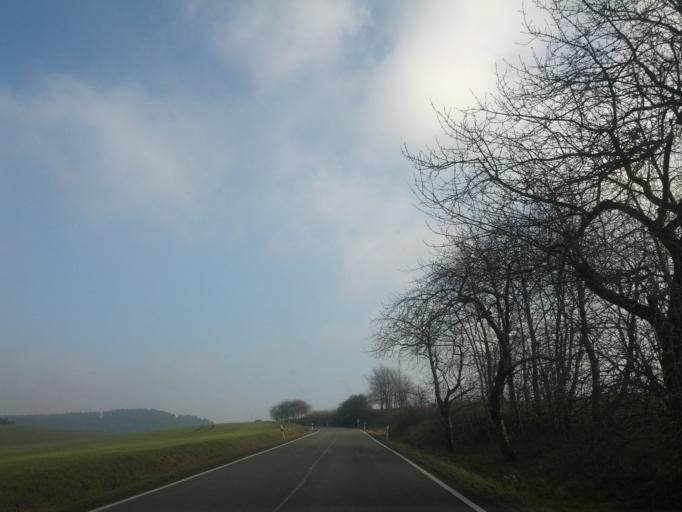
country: DE
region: Thuringia
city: Treffurt
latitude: 51.1247
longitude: 10.2537
